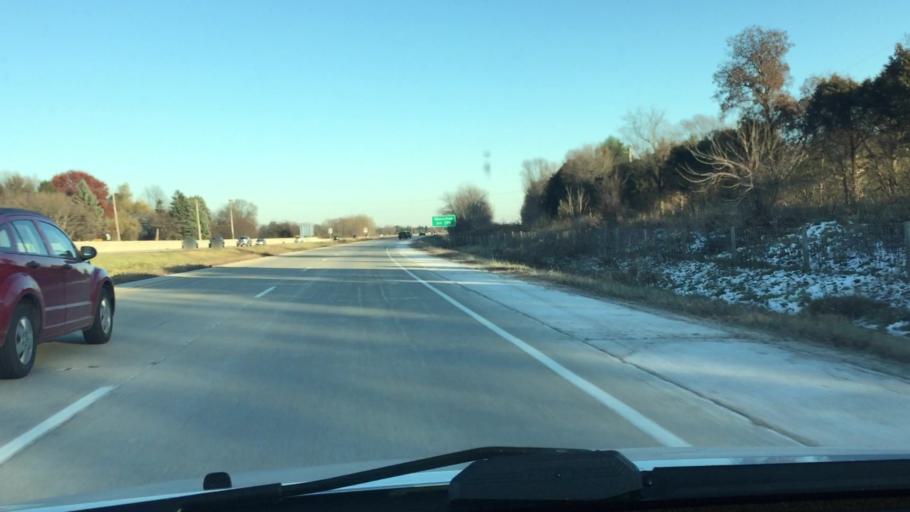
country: US
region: Wisconsin
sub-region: Waukesha County
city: Okauchee Lake
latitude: 43.1088
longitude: -88.4457
